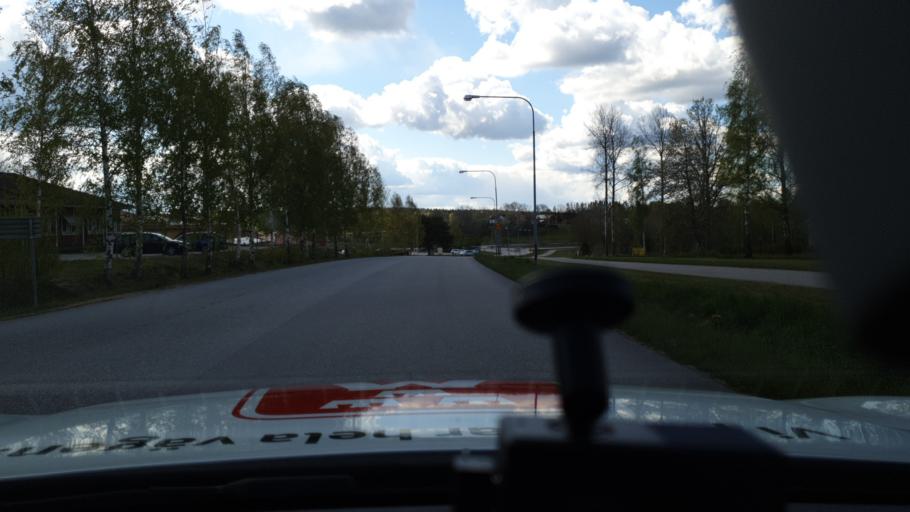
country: SE
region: Kalmar
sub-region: Vimmerby Kommun
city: Vimmerby
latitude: 57.6633
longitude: 15.8761
